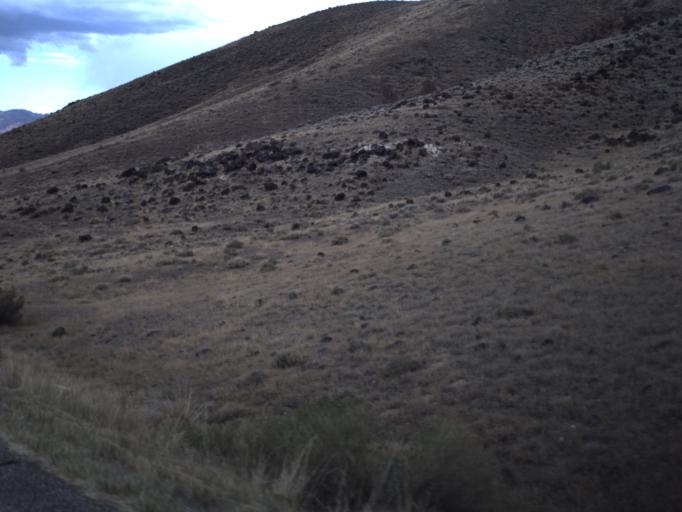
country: US
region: Utah
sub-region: Sevier County
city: Richfield
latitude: 38.7715
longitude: -111.9828
